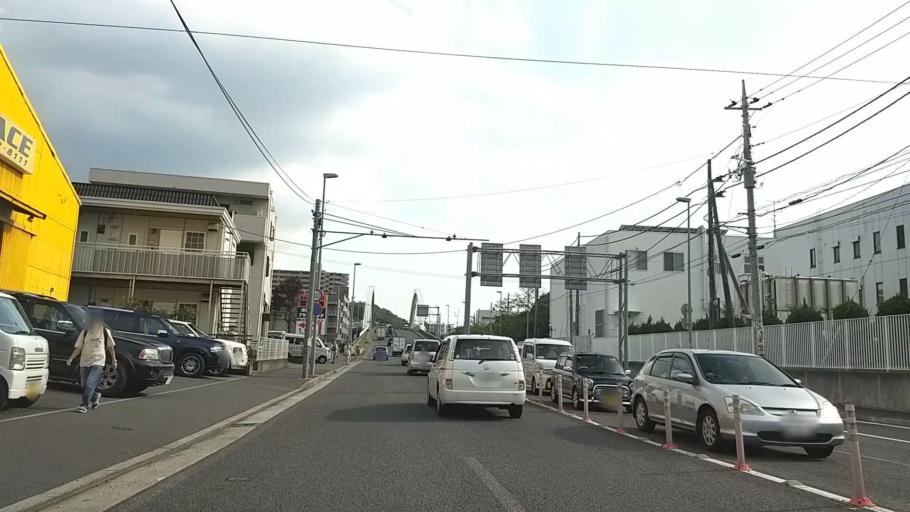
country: JP
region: Kanagawa
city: Yokohama
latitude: 35.5149
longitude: 139.5638
